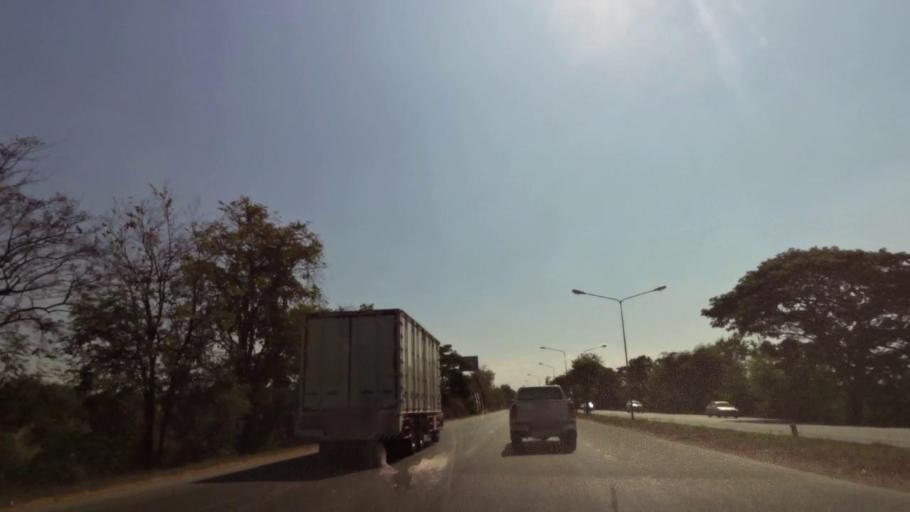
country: TH
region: Nakhon Sawan
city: Kao Liao
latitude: 15.7978
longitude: 100.1205
